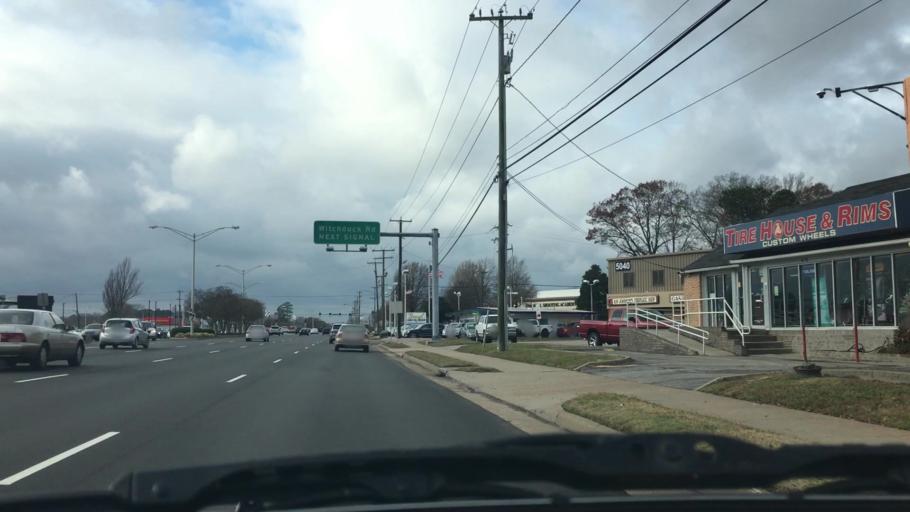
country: US
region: Virginia
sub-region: City of Chesapeake
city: Chesapeake
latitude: 36.8446
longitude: -76.1534
